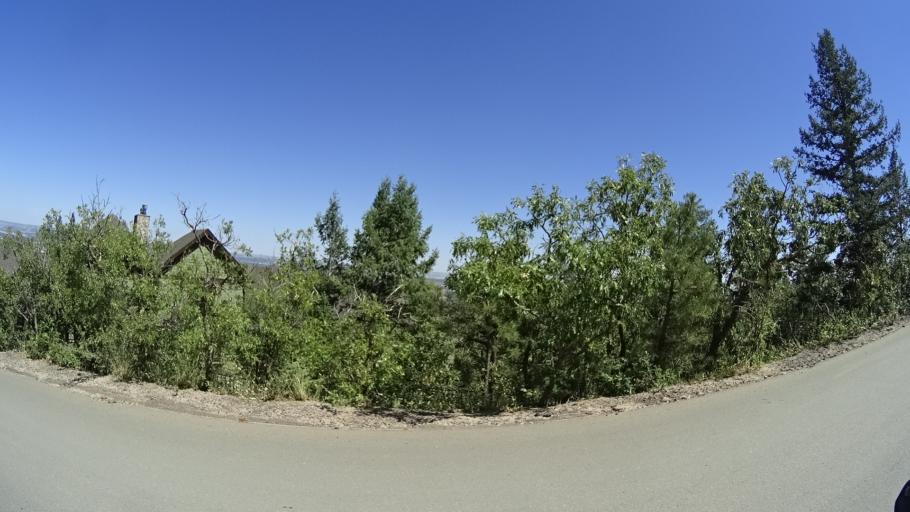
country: US
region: Colorado
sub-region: El Paso County
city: Colorado Springs
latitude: 38.7792
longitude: -104.8634
